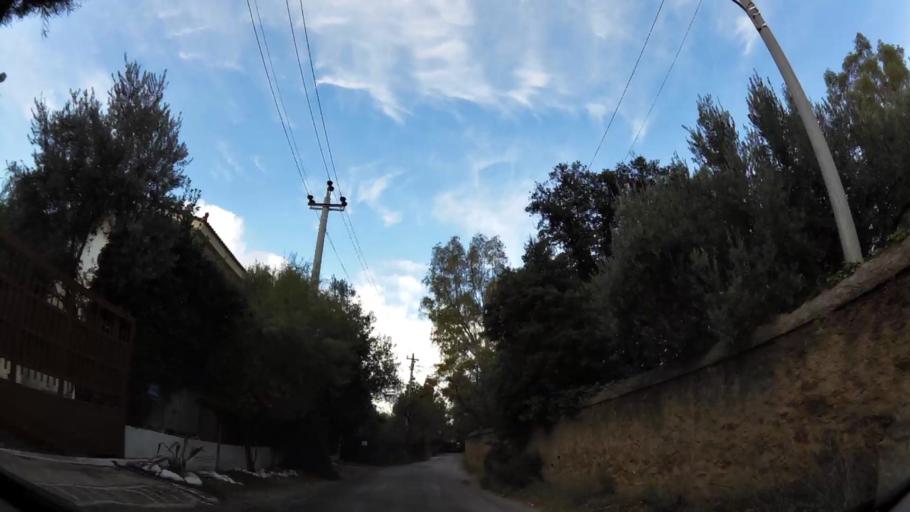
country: GR
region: Attica
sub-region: Nomarchia Athinas
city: Melissia
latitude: 38.0457
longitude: 23.8268
